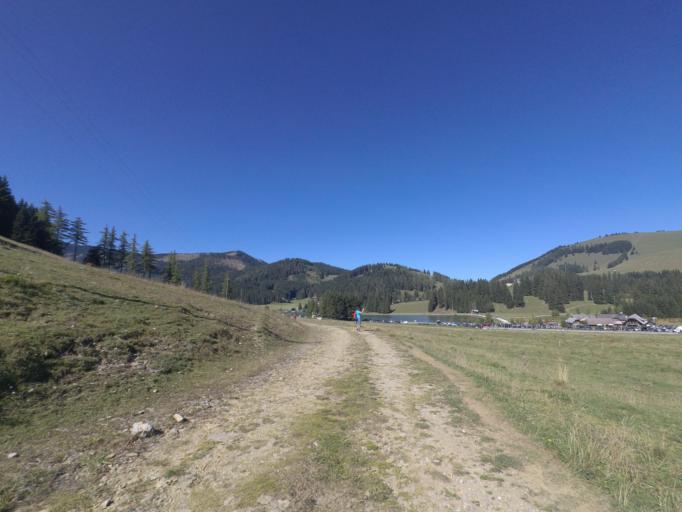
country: AT
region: Styria
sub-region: Politischer Bezirk Weiz
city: Passail
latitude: 47.3458
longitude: 15.4639
